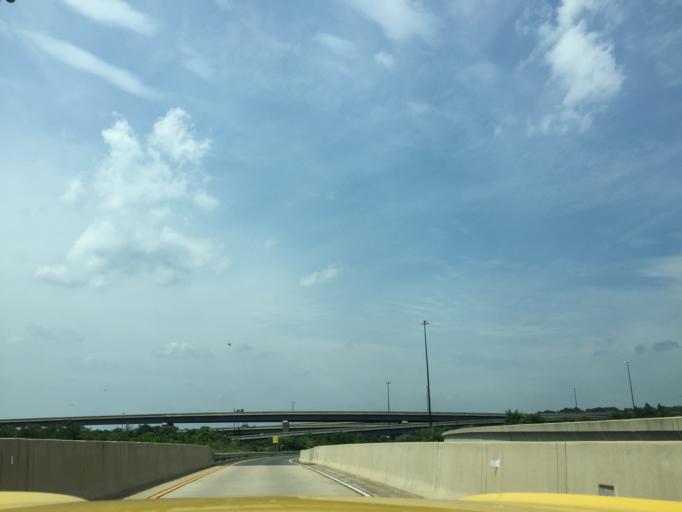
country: US
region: Maryland
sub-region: Prince George's County
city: Forest Heights
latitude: 38.7921
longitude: -77.0135
